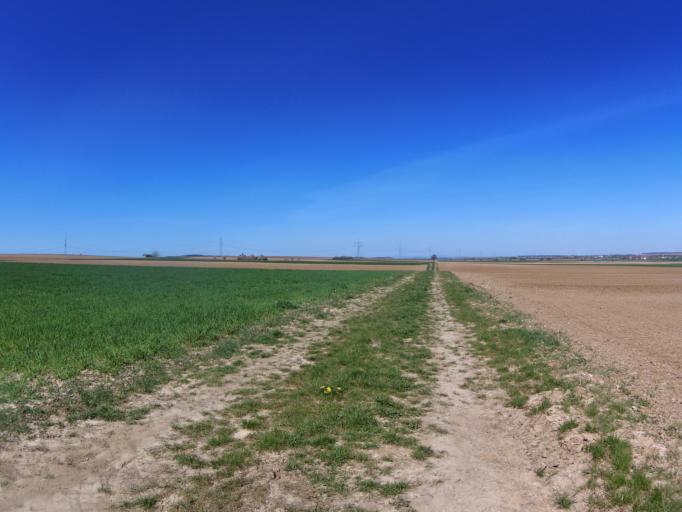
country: DE
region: Bavaria
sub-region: Regierungsbezirk Unterfranken
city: Biebelried
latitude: 49.8019
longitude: 10.0891
